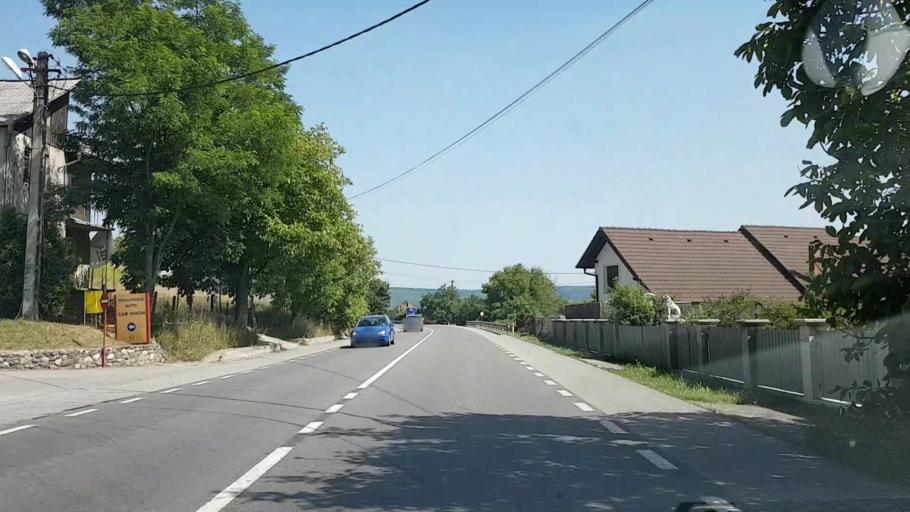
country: RO
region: Bistrita-Nasaud
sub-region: Comuna Beclean
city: Beclean
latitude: 47.1808
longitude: 24.1397
